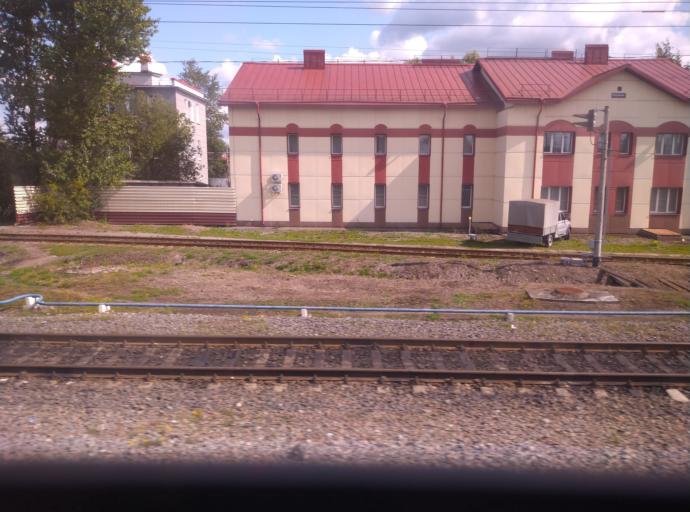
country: RU
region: St.-Petersburg
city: Kolpino
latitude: 59.7533
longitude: 30.6089
